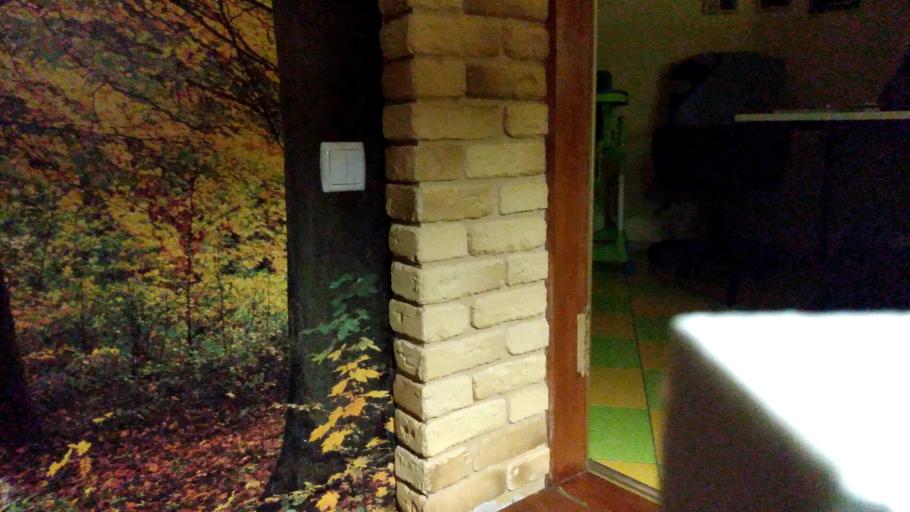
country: RU
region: Vologda
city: Lipin Bor
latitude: 60.9028
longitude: 37.9960
